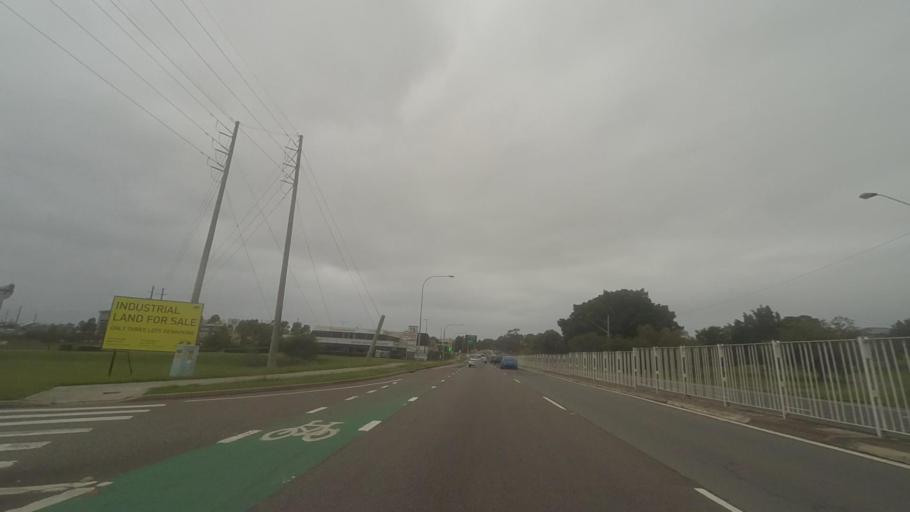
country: AU
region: New South Wales
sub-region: Newcastle
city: Mayfield West
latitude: -32.8842
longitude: 151.7245
